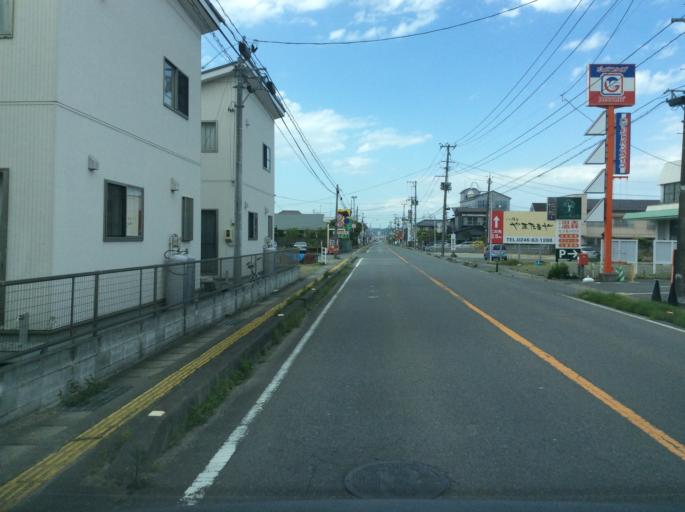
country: JP
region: Ibaraki
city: Kitaibaraki
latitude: 36.8971
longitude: 140.7840
